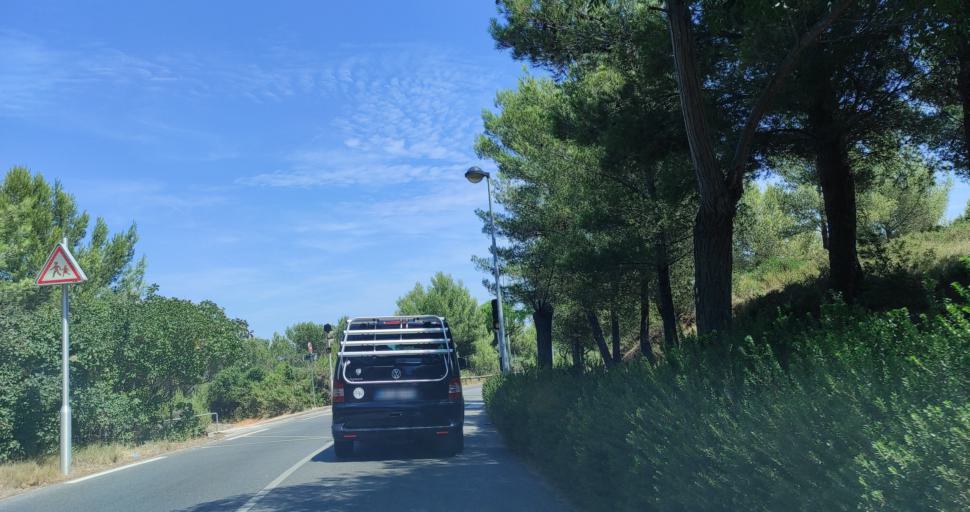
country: FR
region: Provence-Alpes-Cote d'Azur
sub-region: Departement des Bouches-du-Rhone
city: Martigues
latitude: 43.4213
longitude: 5.0444
